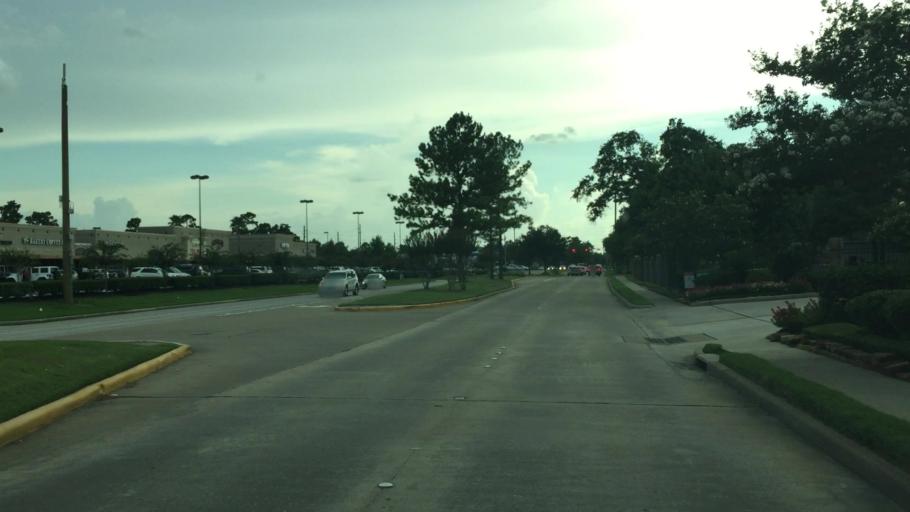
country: US
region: Texas
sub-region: Harris County
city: Hudson
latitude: 30.0121
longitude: -95.5123
